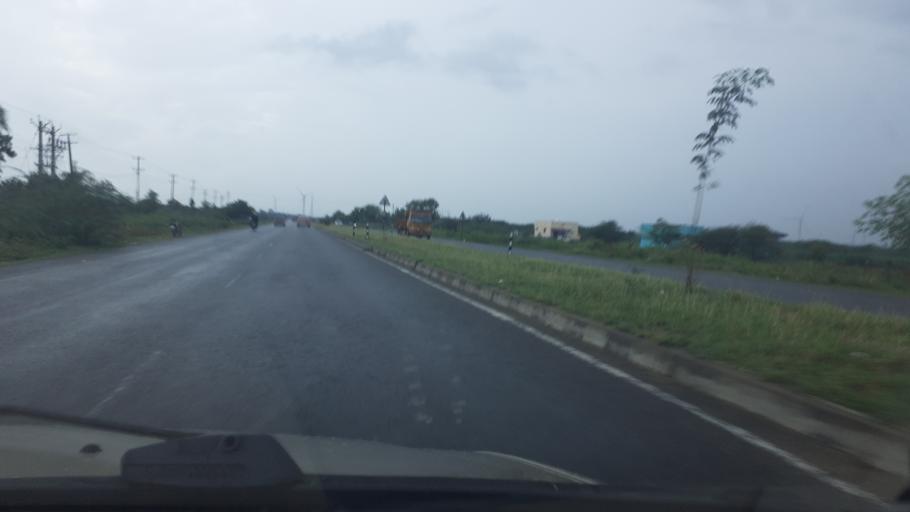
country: IN
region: Tamil Nadu
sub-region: Thoothukkudi
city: Kayattar
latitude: 9.0166
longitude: 77.7857
